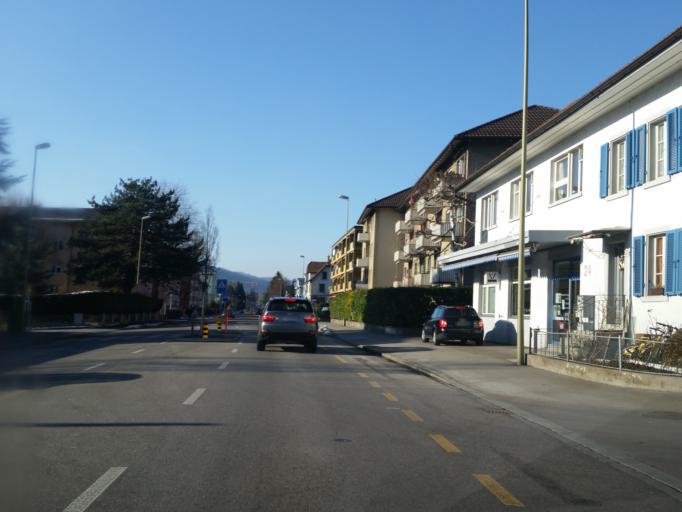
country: CH
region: Zurich
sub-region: Bezirk Dietikon
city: Dietikon / Vorstadt
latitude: 47.4063
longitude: 8.3973
